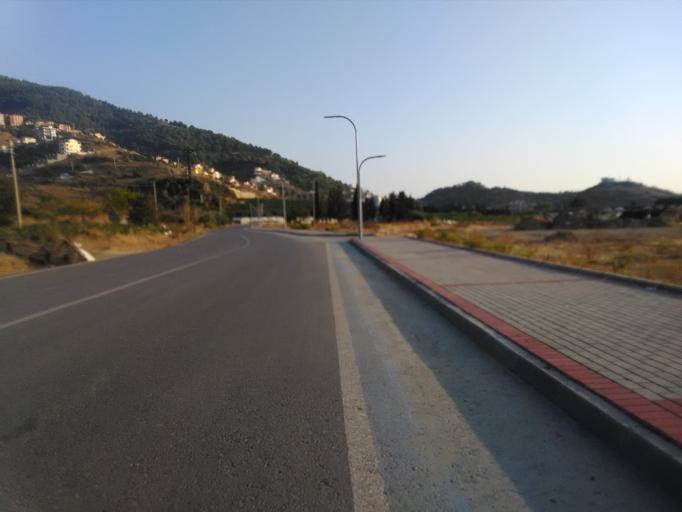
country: TR
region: Antalya
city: Gazipasa
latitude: 36.2429
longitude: 32.2980
